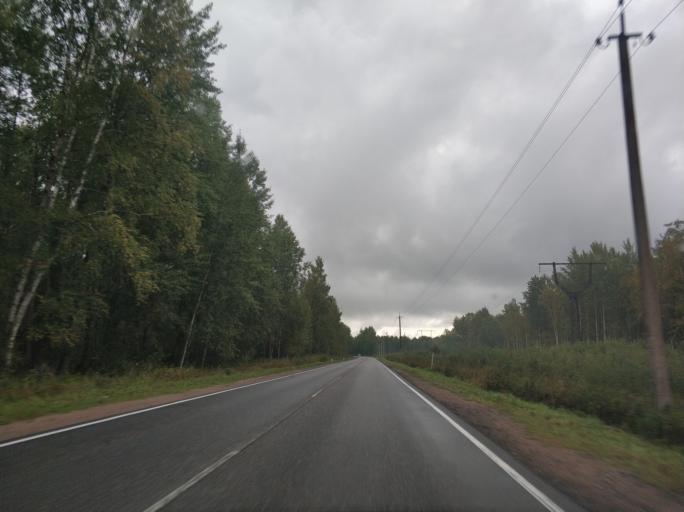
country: RU
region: Leningrad
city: Borisova Griva
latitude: 60.1115
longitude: 30.9619
